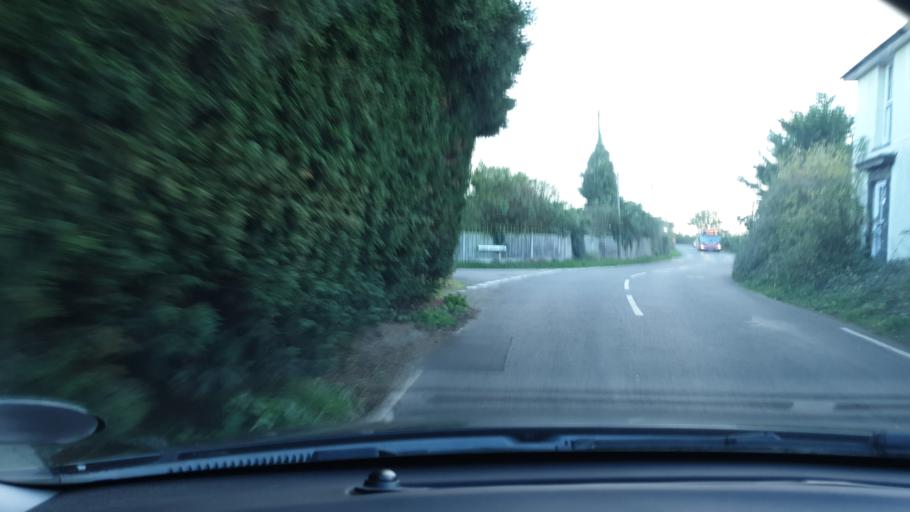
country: GB
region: England
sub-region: Essex
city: Little Clacton
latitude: 51.8963
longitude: 1.1471
